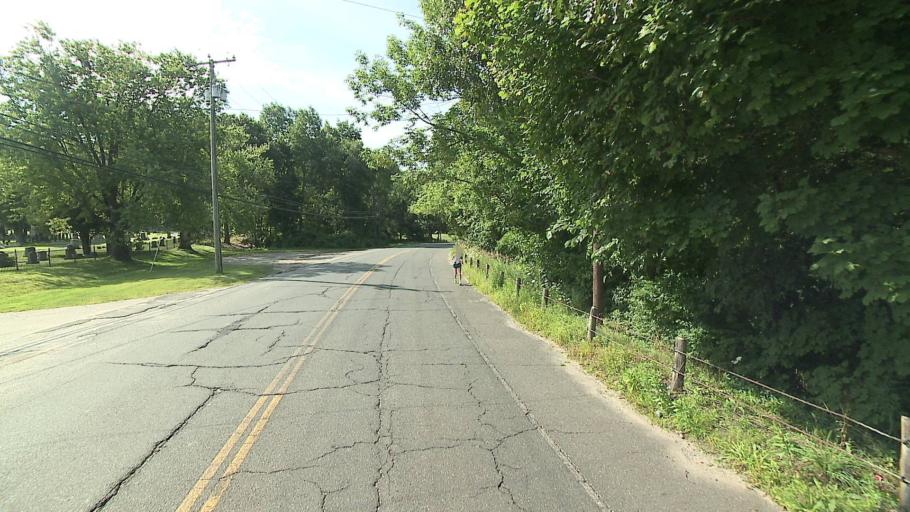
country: US
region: New York
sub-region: Putnam County
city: Putnam Lake
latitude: 41.4805
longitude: -73.4966
